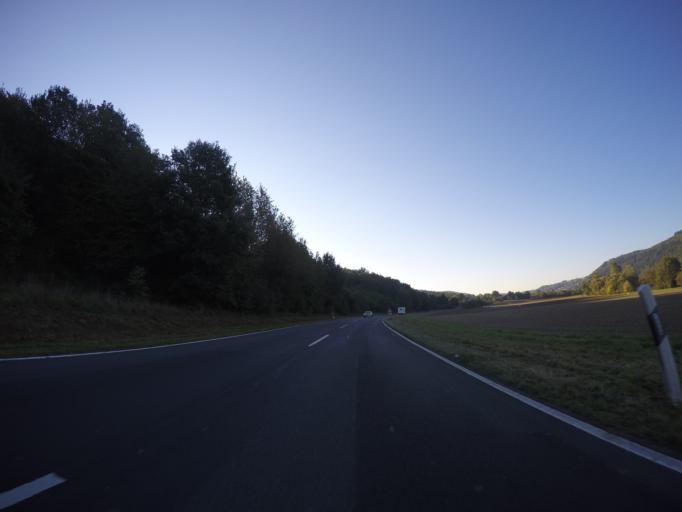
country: DE
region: Bavaria
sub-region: Regierungsbezirk Unterfranken
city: Kreuzwertheim
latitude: 49.7826
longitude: 9.5140
